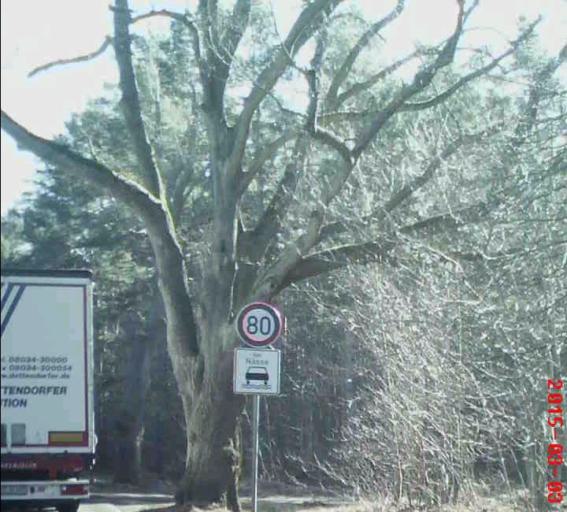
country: DE
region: Thuringia
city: Stadtilm
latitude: 50.7685
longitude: 11.0992
